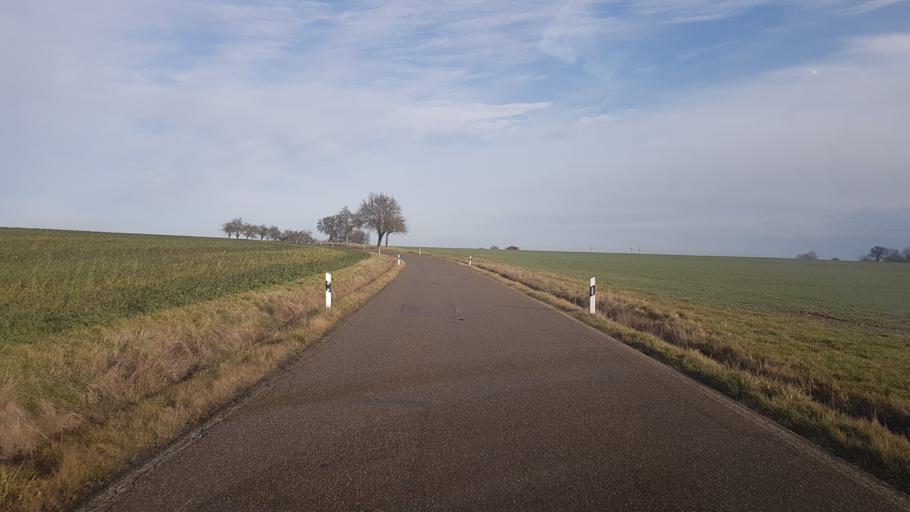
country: DE
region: Baden-Wuerttemberg
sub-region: Regierungsbezirk Stuttgart
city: Langenburg
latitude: 49.2090
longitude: 9.8730
